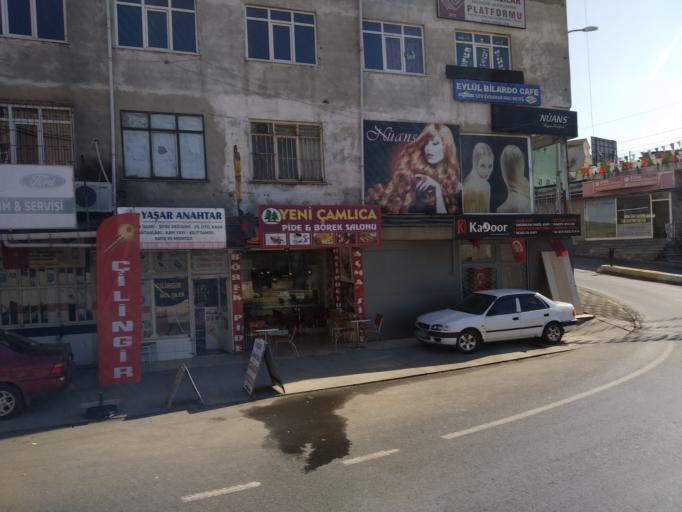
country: TR
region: Istanbul
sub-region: Atasehir
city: Atasehir
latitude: 40.9903
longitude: 29.1599
